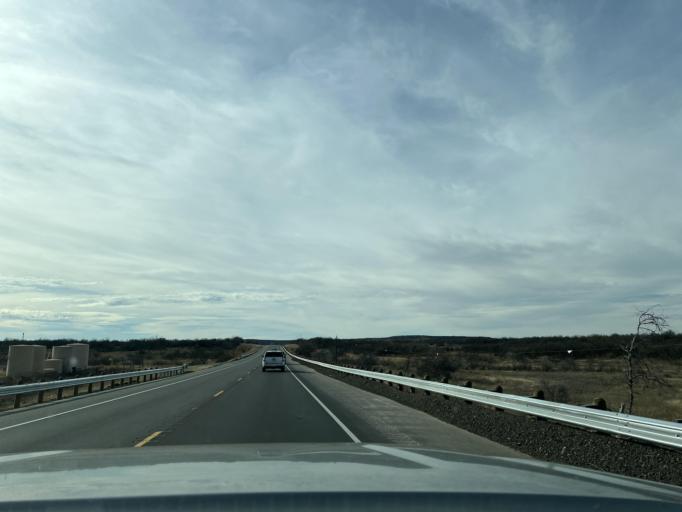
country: US
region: Texas
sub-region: Shackelford County
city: Albany
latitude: 32.7141
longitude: -99.3389
